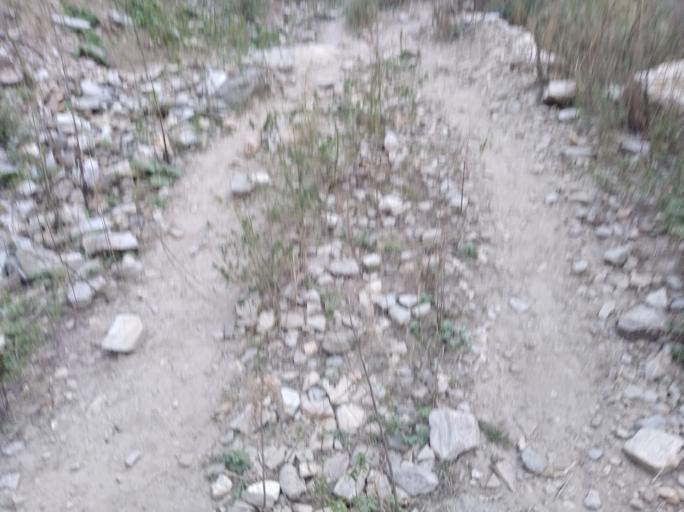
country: NP
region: Western Region
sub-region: Dhawalagiri Zone
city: Jomsom
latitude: 28.9307
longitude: 82.9624
